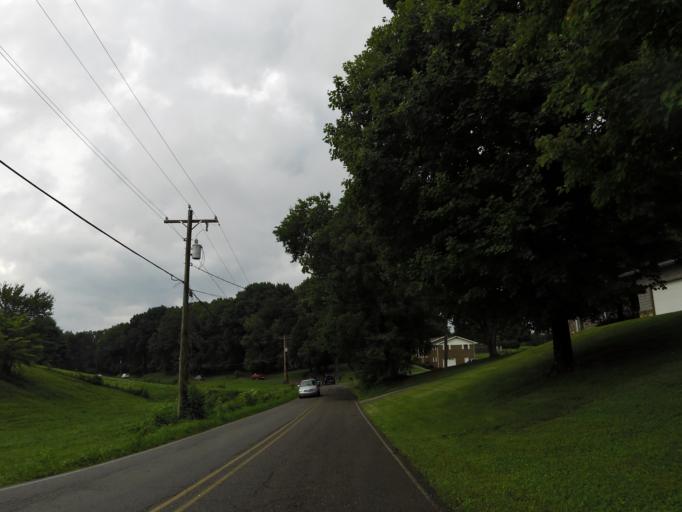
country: US
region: Tennessee
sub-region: Blount County
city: Wildwood
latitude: 35.7829
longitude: -83.8973
